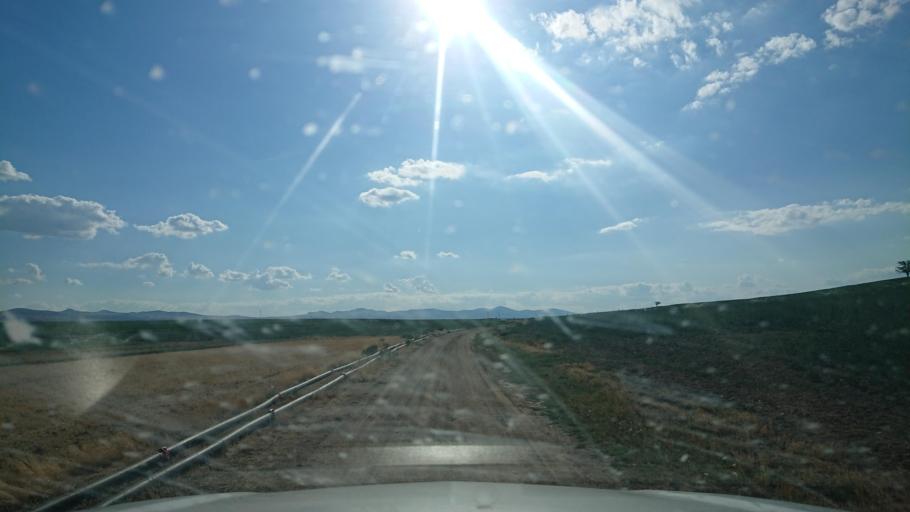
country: TR
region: Aksaray
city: Sariyahsi
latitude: 39.0193
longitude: 33.8922
